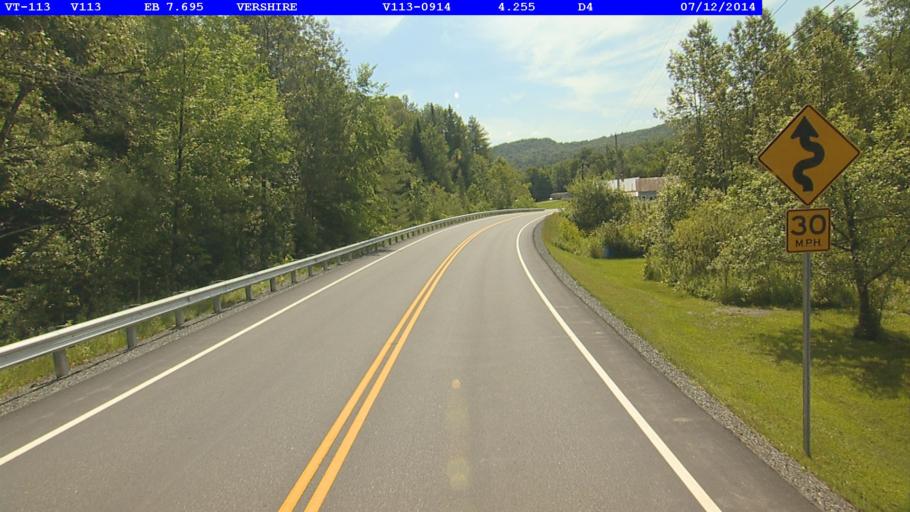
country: US
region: Vermont
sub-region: Orange County
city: Chelsea
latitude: 43.9655
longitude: -72.3106
